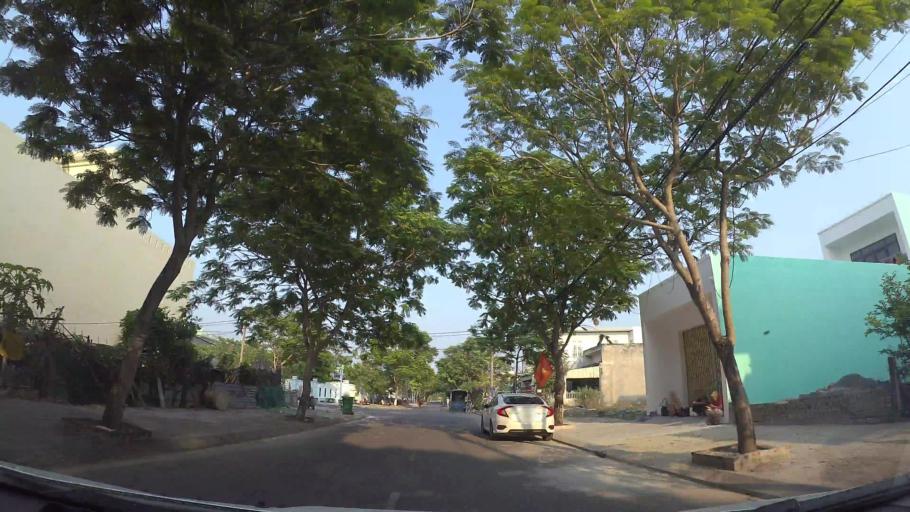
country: VN
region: Da Nang
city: Ngu Hanh Son
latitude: 15.9791
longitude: 108.2510
